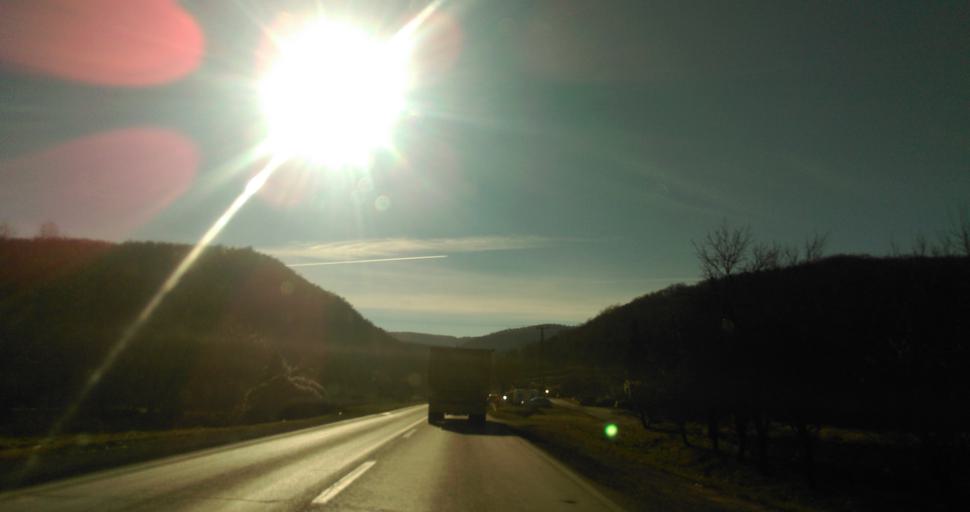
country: RS
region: Autonomna Pokrajina Vojvodina
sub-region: Juznobacki Okrug
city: Novi Sad
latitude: 45.1894
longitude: 19.8404
